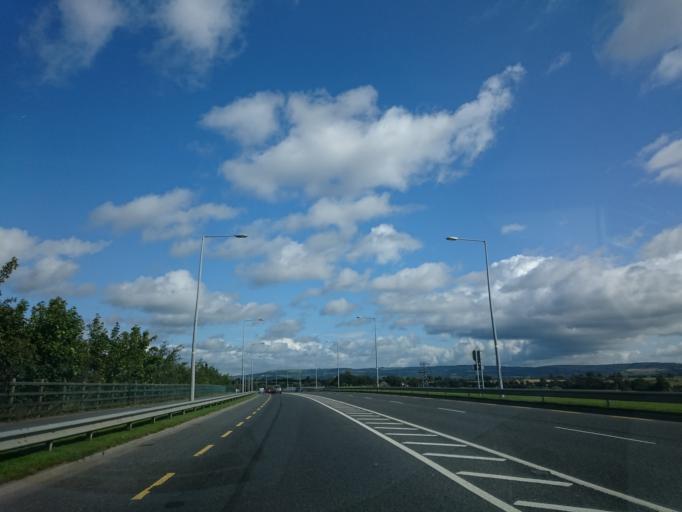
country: IE
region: Leinster
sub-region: Kilkenny
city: Kilkenny
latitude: 52.6532
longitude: -7.2266
